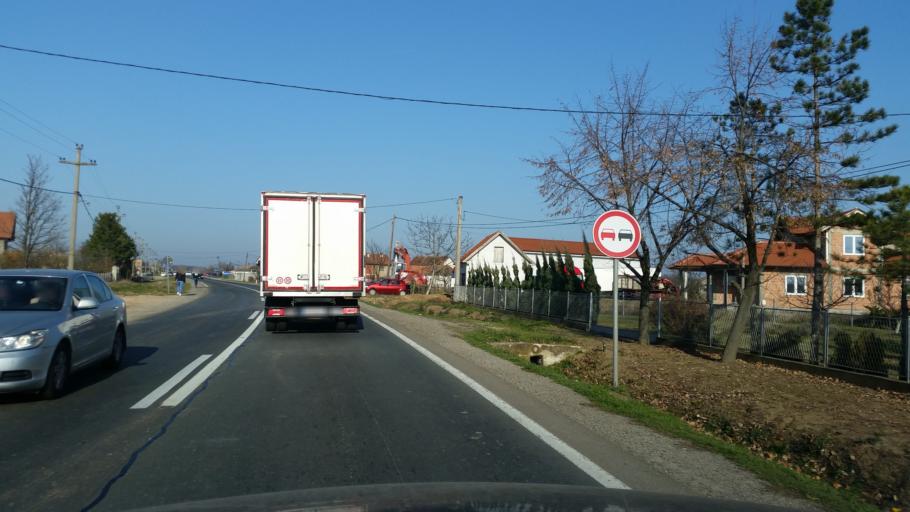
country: RS
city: Stepojevac
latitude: 44.5330
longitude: 20.2981
